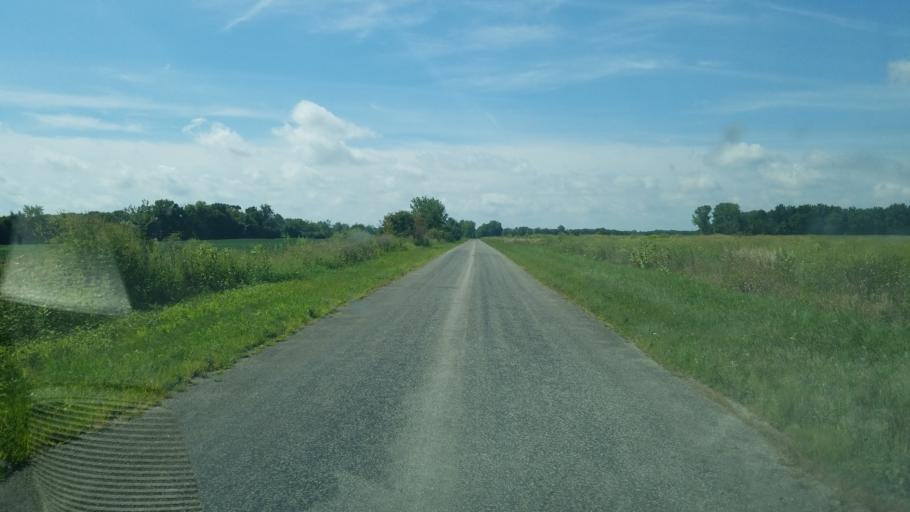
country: US
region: Ohio
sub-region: Hardin County
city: Kenton
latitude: 40.6085
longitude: -83.6447
